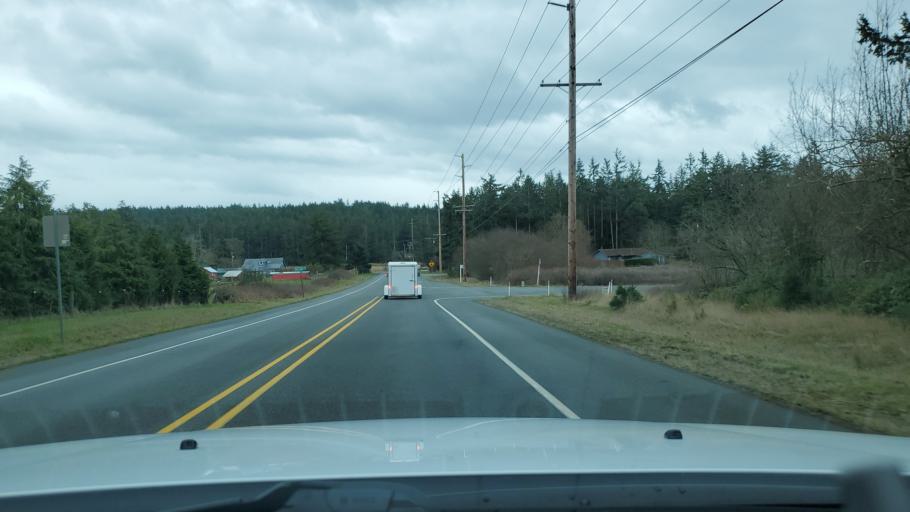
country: US
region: Washington
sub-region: Island County
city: Coupeville
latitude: 48.2343
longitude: -122.7519
